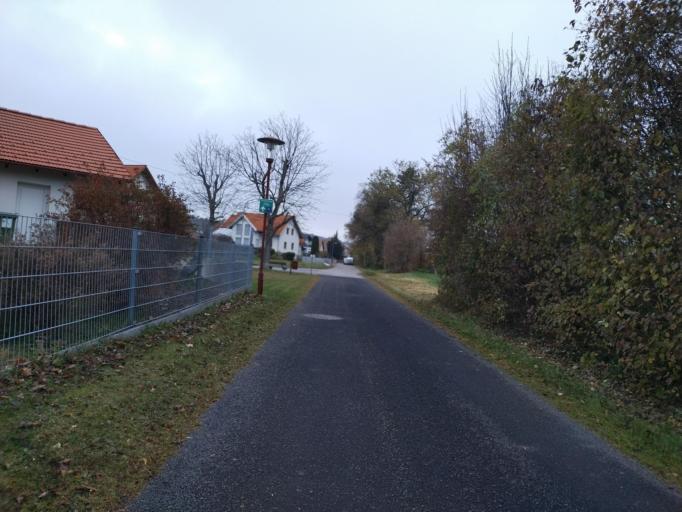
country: AT
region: Lower Austria
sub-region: Politischer Bezirk Neunkirchen
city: Pitten
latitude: 47.7103
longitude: 16.1755
